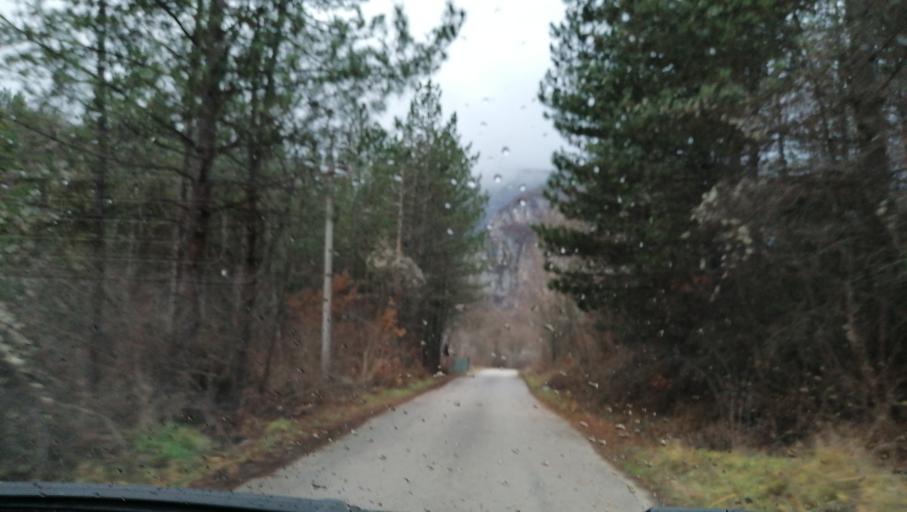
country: RS
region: Central Serbia
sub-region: Pirotski Okrug
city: Dimitrovgrad
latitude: 42.9817
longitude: 22.6439
